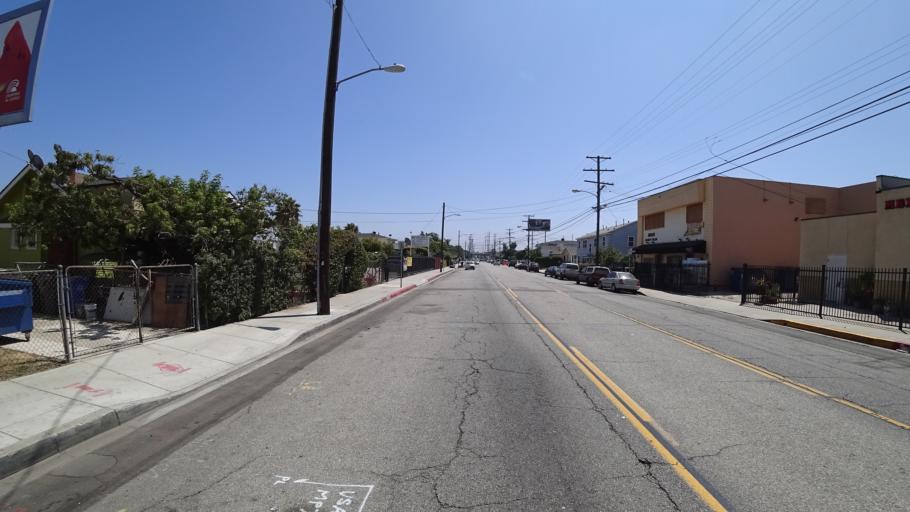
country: US
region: California
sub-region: Los Angeles County
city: Lennox
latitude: 33.9370
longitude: -118.3613
